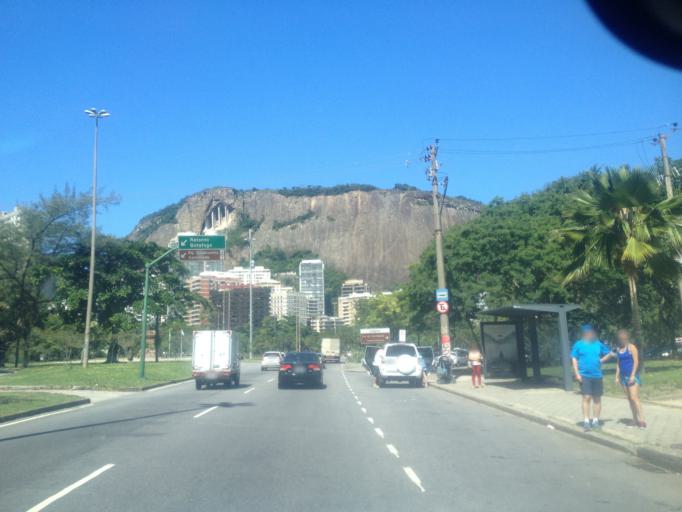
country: BR
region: Rio de Janeiro
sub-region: Rio De Janeiro
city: Rio de Janeiro
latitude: -22.9740
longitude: -43.2014
